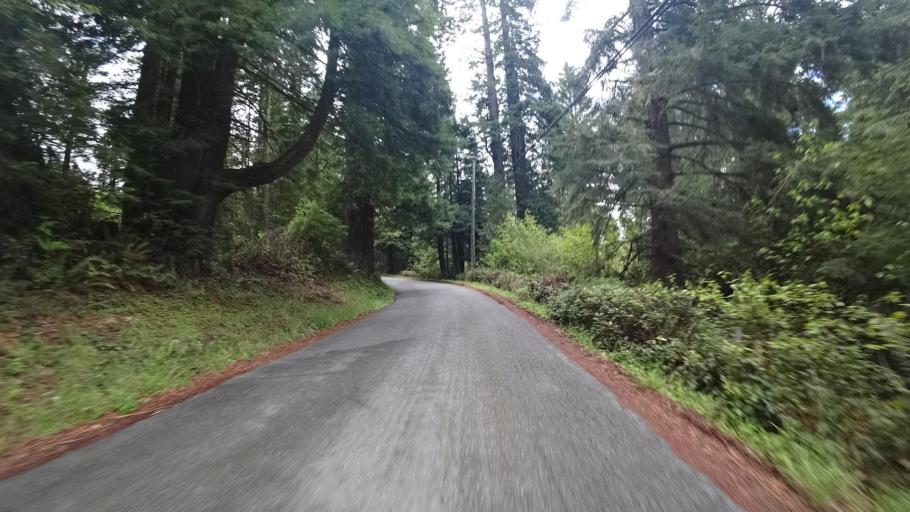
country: US
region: California
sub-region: Humboldt County
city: Bayside
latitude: 40.8482
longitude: -124.0279
